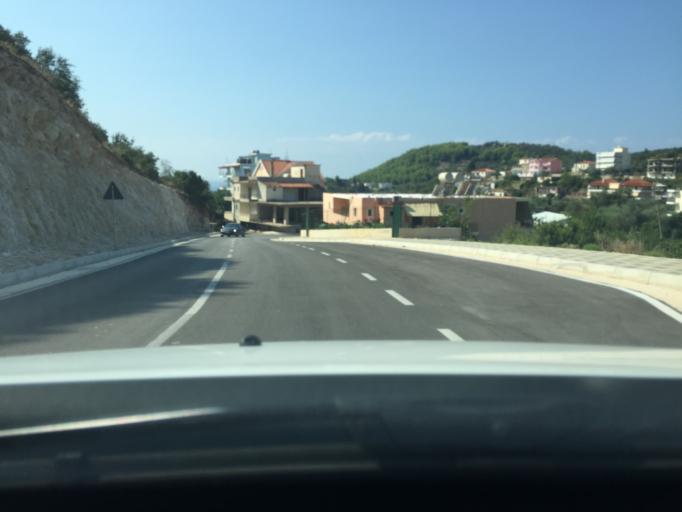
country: AL
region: Vlore
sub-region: Rrethi i Vlores
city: Himare
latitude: 40.1104
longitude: 19.7438
